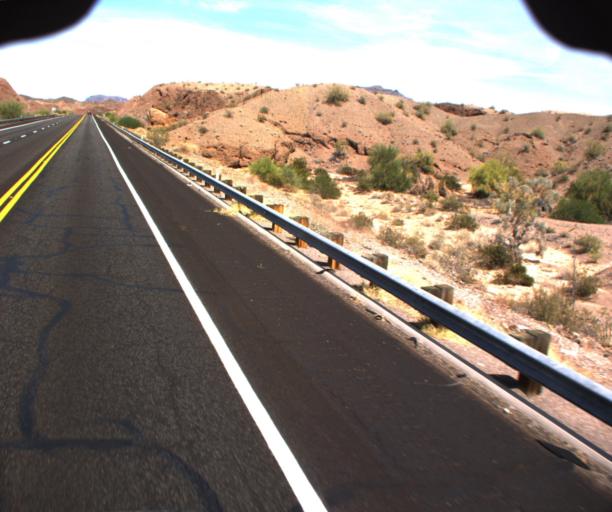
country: US
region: Arizona
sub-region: La Paz County
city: Cienega Springs
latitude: 34.2197
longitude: -114.1909
